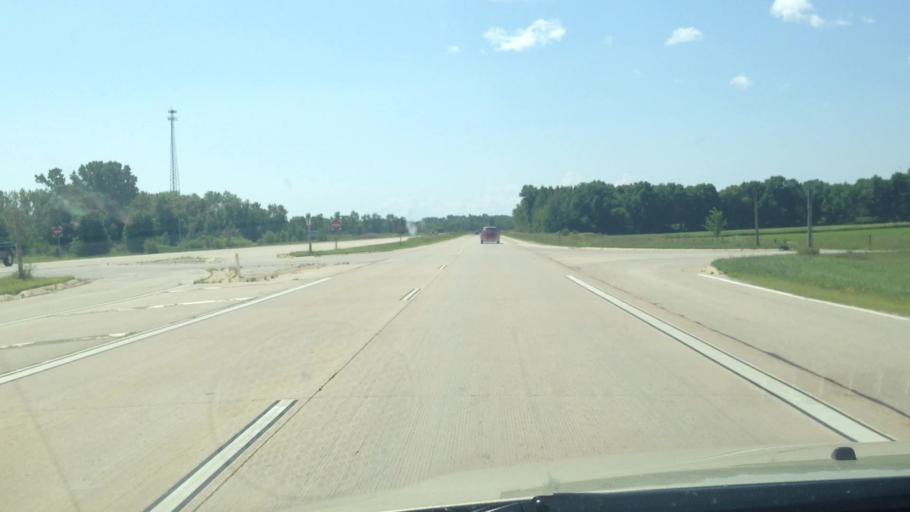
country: US
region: Wisconsin
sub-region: Oconto County
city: Oconto
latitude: 44.9359
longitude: -87.8704
